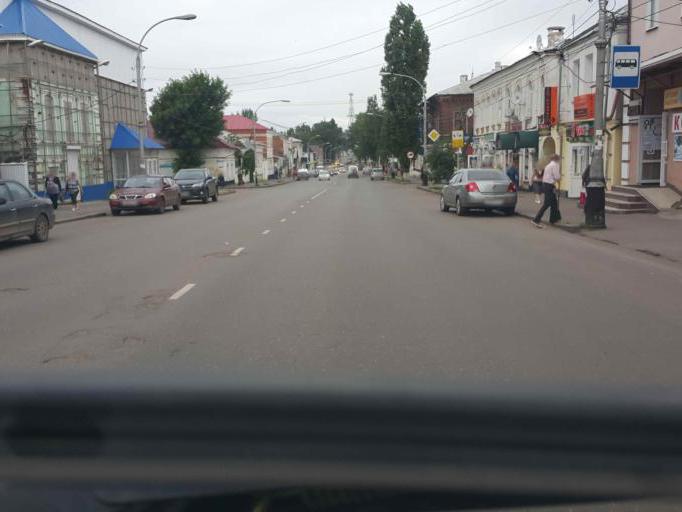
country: RU
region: Tambov
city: Michurinsk
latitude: 52.8896
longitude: 40.5074
